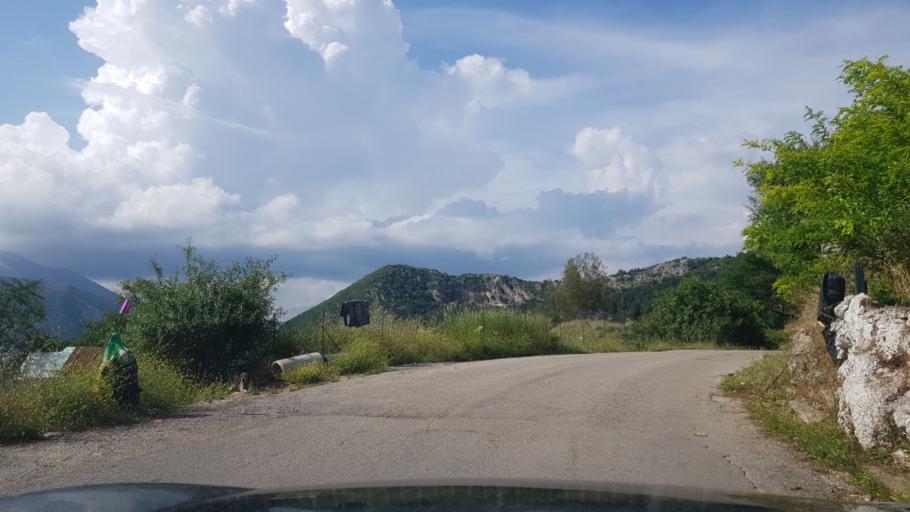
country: GR
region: Ionian Islands
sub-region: Lefkada
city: Nidri
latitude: 38.6454
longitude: 20.7072
